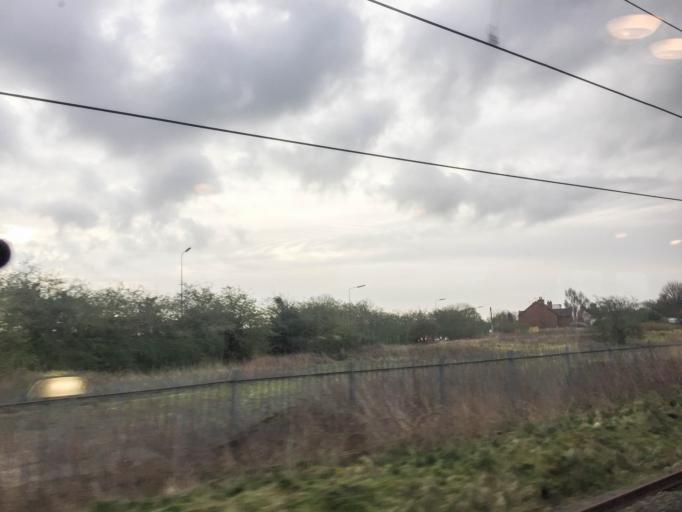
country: GB
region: England
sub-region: Staffordshire
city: Stafford
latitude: 52.7740
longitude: -2.1109
